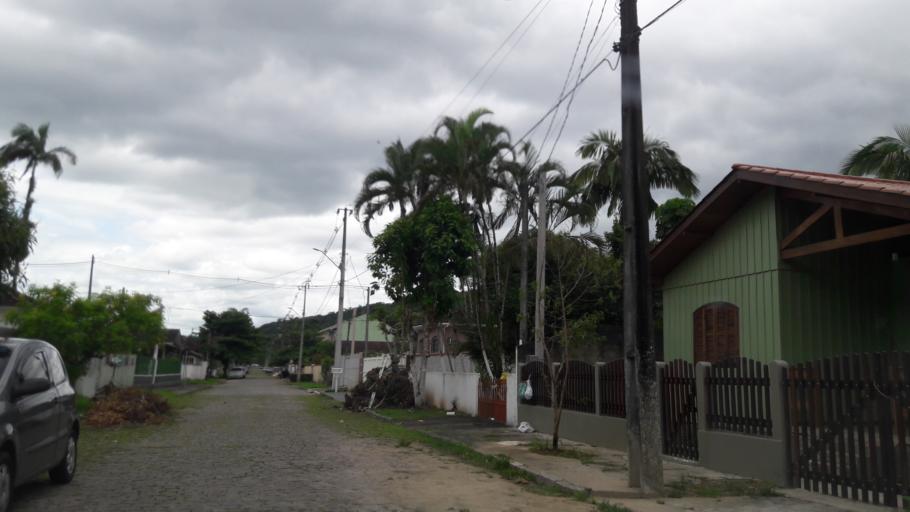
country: BR
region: Parana
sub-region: Antonina
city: Antonina
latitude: -25.4749
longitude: -48.8316
